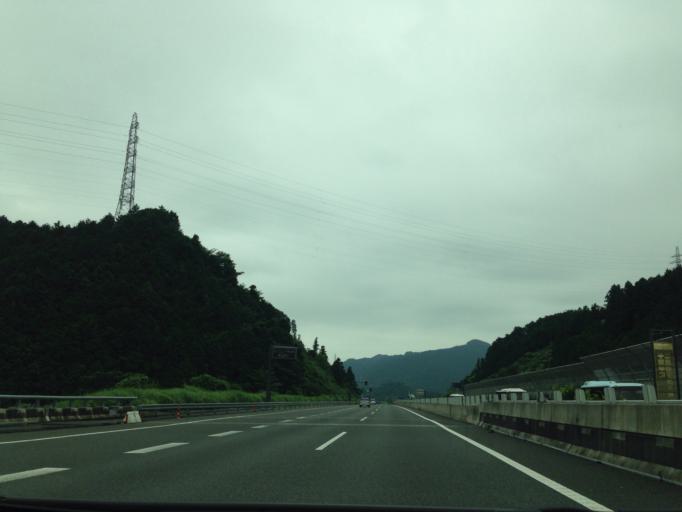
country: JP
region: Shizuoka
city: Fujinomiya
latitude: 35.1422
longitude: 138.5183
